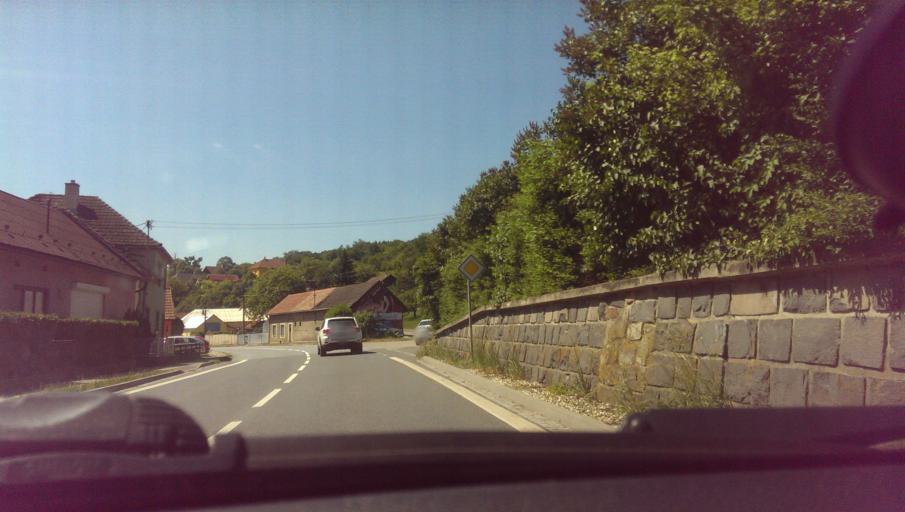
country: CZ
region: Zlin
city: Brezolupy
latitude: 49.1482
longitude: 17.6061
